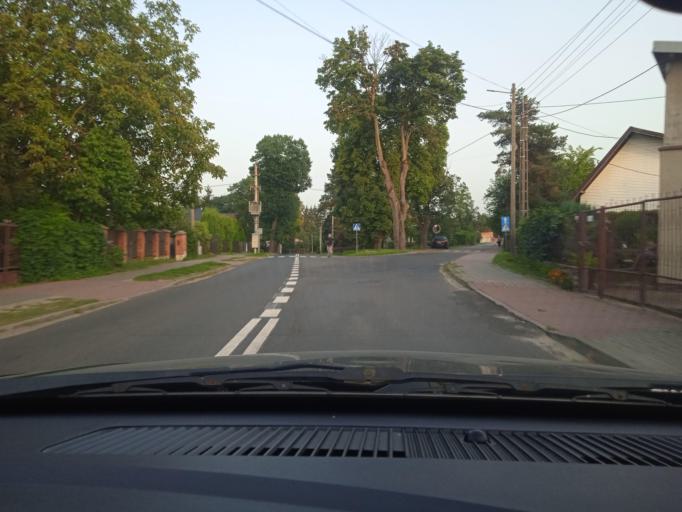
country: PL
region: Masovian Voivodeship
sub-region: Powiat nowodworski
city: Pomiechowek
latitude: 52.4738
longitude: 20.7274
